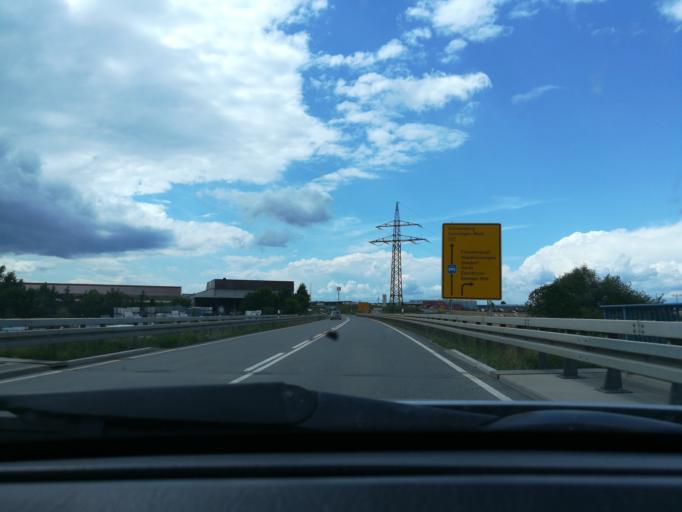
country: DE
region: Baden-Wuerttemberg
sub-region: Freiburg Region
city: Dunningen
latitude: 48.2213
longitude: 8.5072
